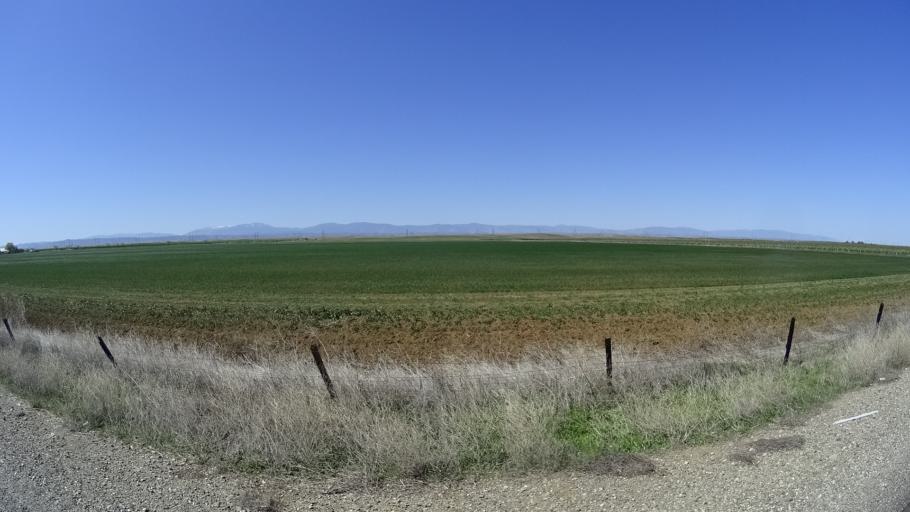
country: US
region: California
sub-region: Glenn County
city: Willows
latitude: 39.5811
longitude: -122.2496
